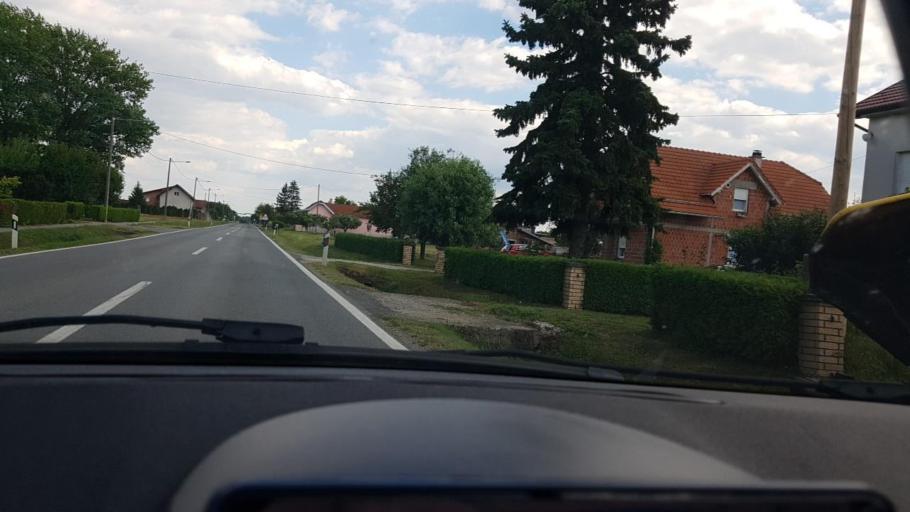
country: HR
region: Bjelovarsko-Bilogorska
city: Zdralovi
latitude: 45.8381
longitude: 16.9549
